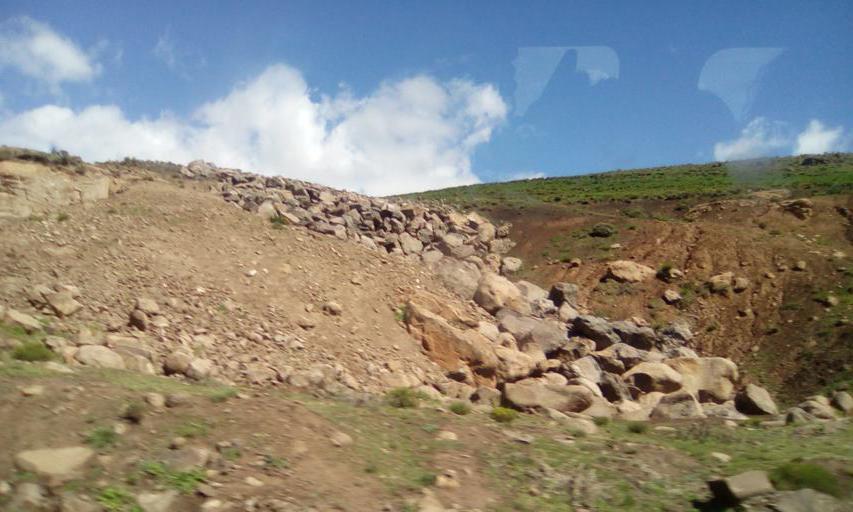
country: LS
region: Maseru
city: Nako
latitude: -29.8186
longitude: 28.0333
